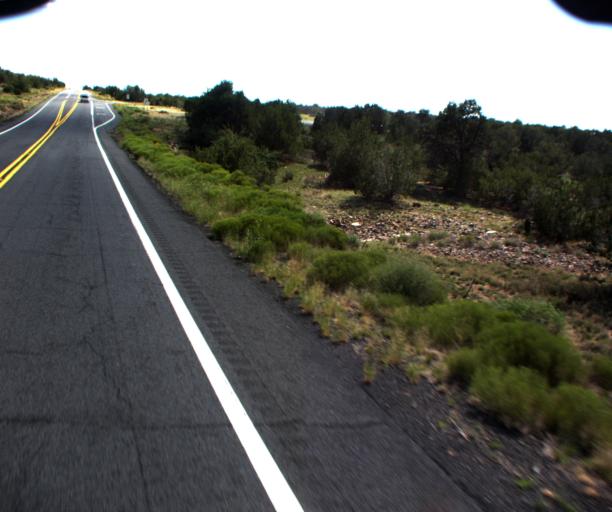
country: US
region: Arizona
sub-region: Coconino County
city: Williams
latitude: 35.4844
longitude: -112.1757
